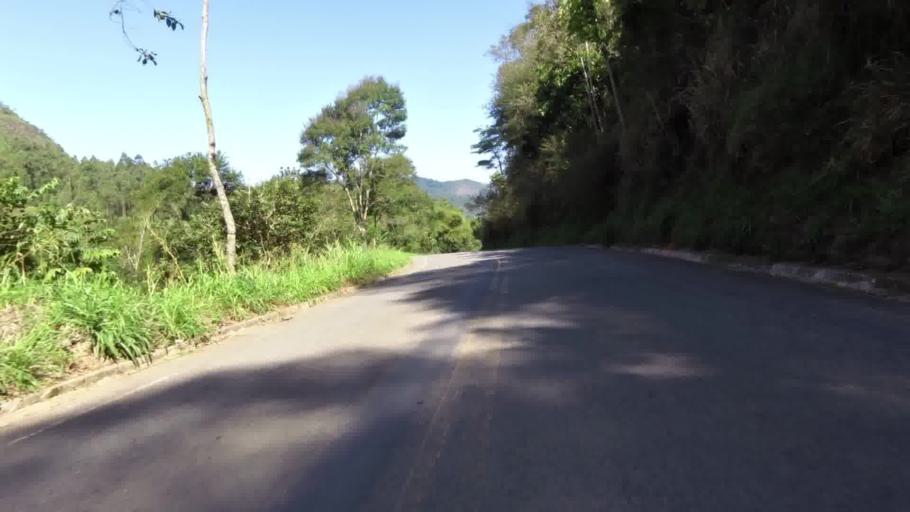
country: BR
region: Espirito Santo
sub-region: Alfredo Chaves
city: Alfredo Chaves
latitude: -20.5059
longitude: -40.7764
